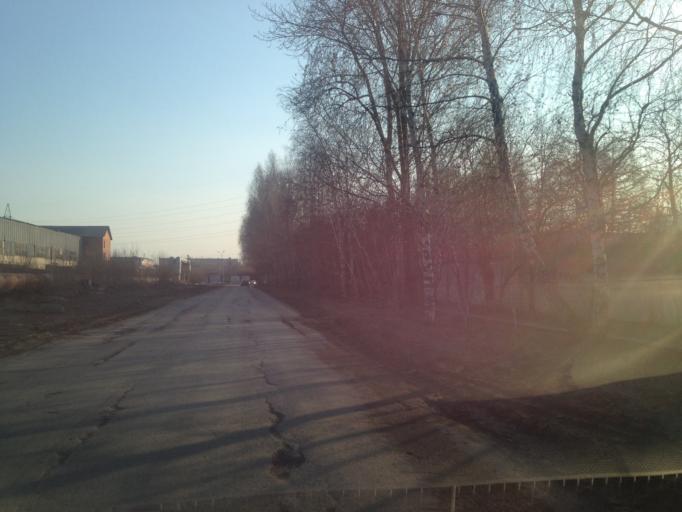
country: RU
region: Sverdlovsk
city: Yekaterinburg
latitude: 56.8756
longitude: 60.5439
